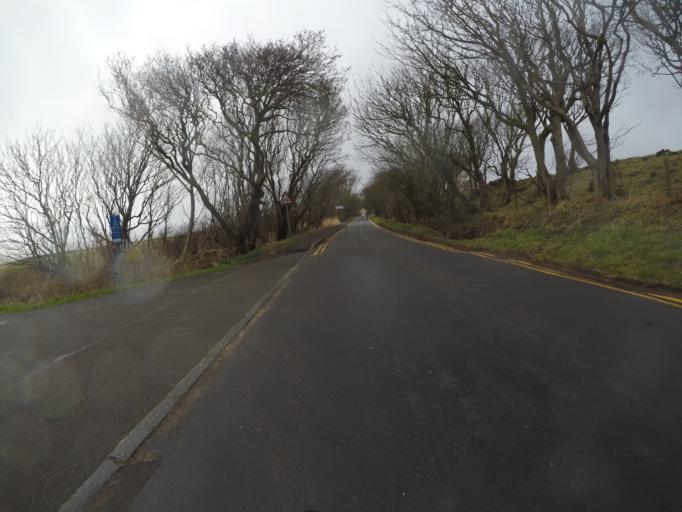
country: GB
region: Scotland
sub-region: North Ayrshire
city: West Kilbride
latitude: 55.6970
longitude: -4.8873
